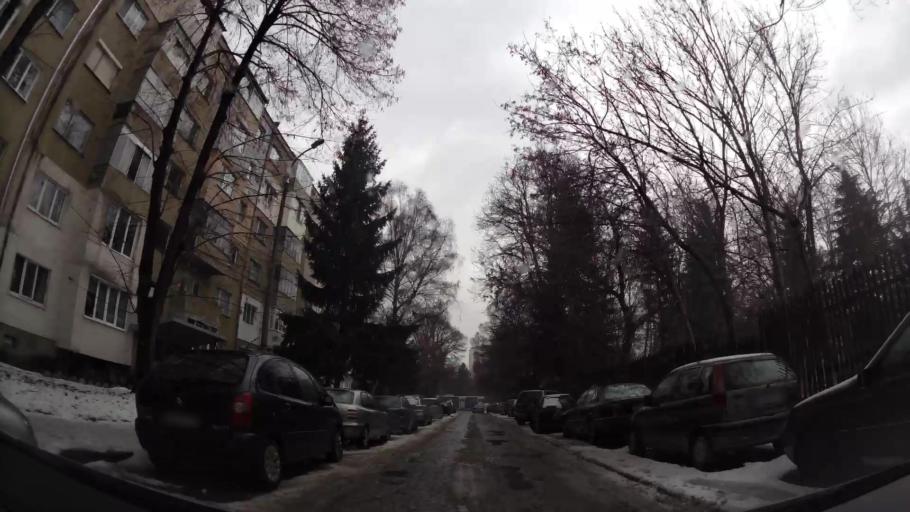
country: BG
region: Sofia-Capital
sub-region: Stolichna Obshtina
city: Sofia
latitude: 42.6696
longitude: 23.2826
